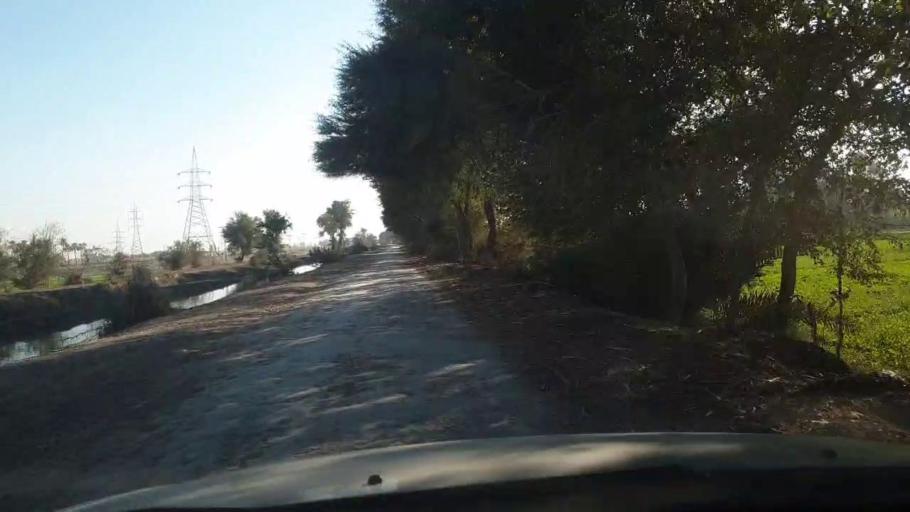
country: PK
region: Sindh
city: Ghotki
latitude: 28.0379
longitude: 69.3240
